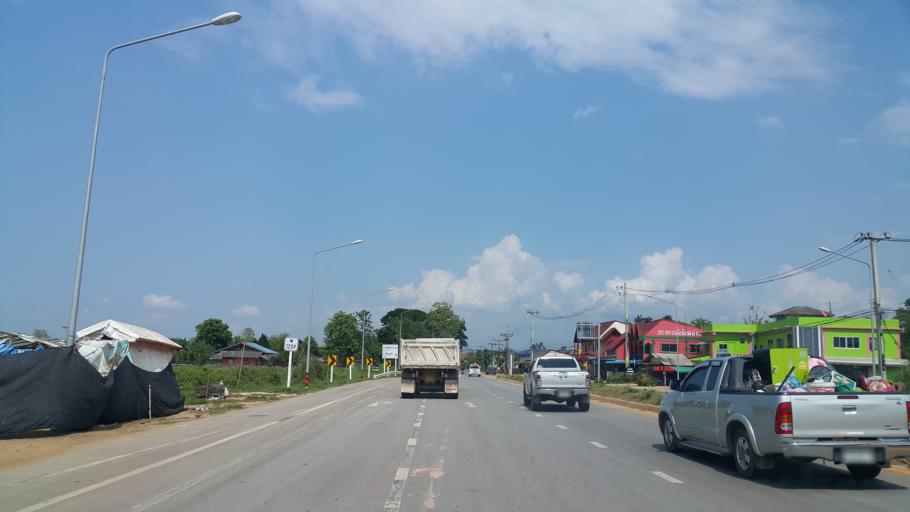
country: TH
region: Chiang Rai
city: Chiang Rai
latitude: 20.0052
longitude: 99.8938
